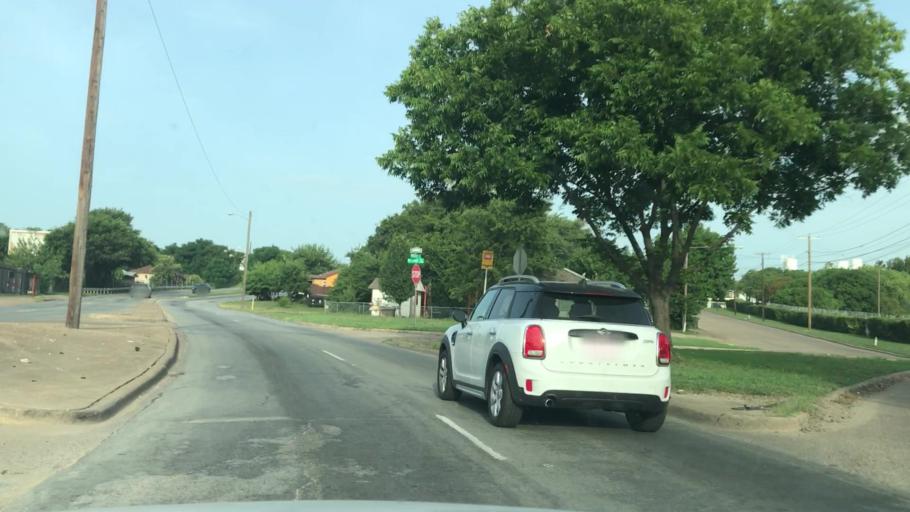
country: US
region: Texas
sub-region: Dallas County
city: Dallas
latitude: 32.7836
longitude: -96.7344
